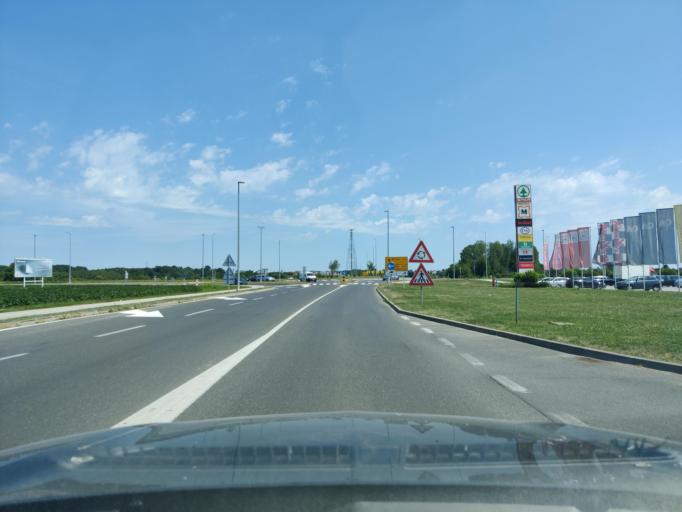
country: HR
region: Medimurska
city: Cakovec
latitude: 46.3964
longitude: 16.4274
